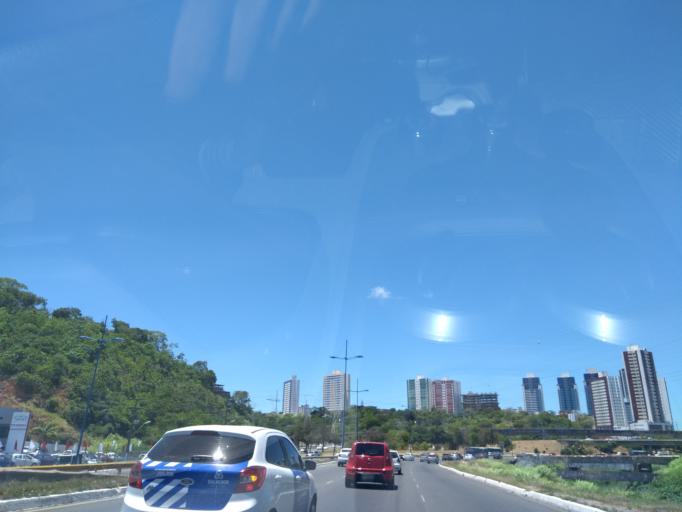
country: BR
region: Bahia
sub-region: Salvador
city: Salvador
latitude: -12.9773
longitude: -38.4744
